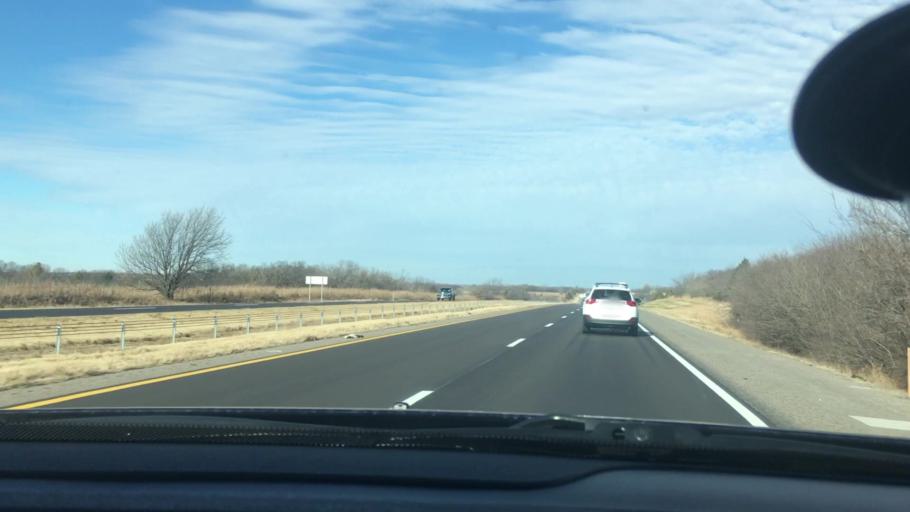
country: US
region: Oklahoma
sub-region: Cleveland County
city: Noble
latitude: 35.0972
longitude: -97.4248
